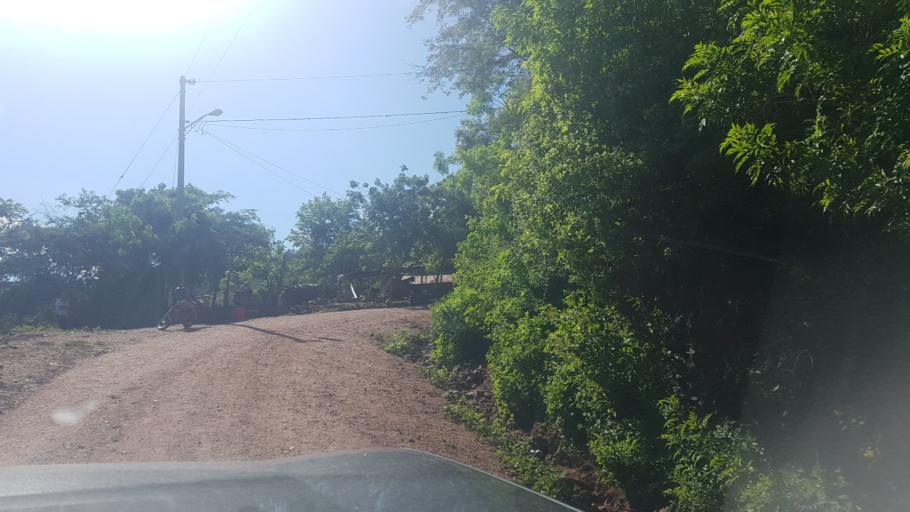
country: NI
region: Nueva Segovia
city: Ocotal
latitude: 13.6372
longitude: -86.6253
